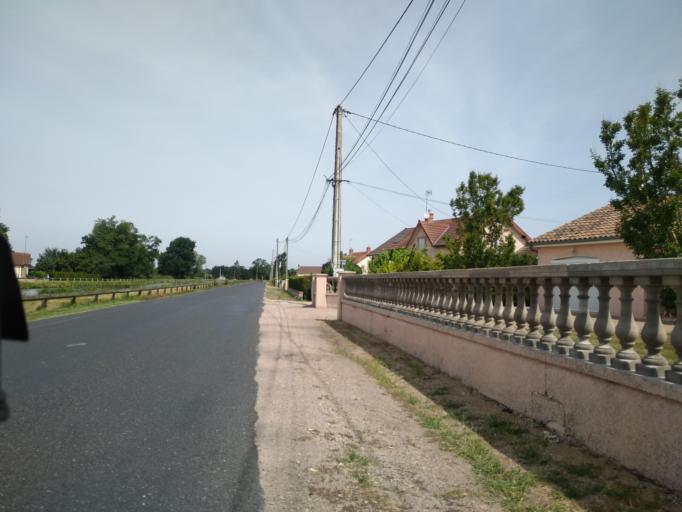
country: FR
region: Auvergne
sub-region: Departement de l'Allier
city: Molinet
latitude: 46.4547
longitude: 3.9658
